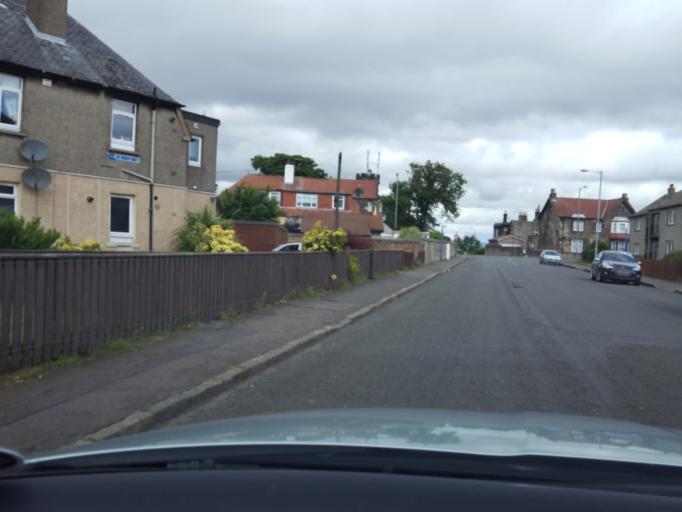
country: GB
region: Scotland
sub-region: Falkirk
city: Bo'ness
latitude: 56.0112
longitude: -3.6060
